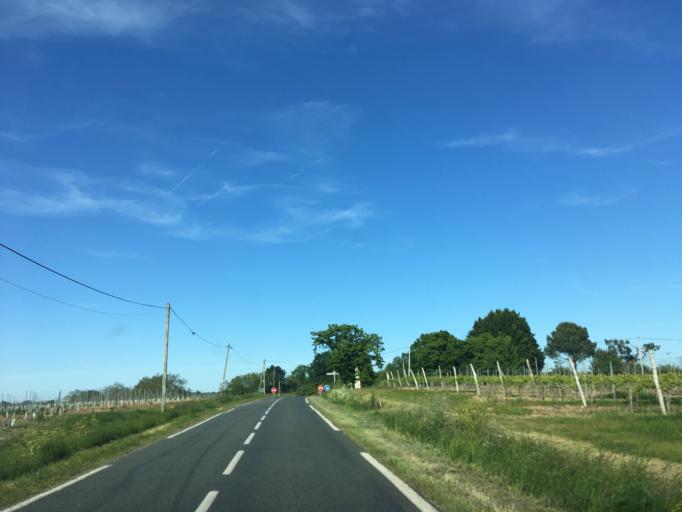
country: FR
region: Poitou-Charentes
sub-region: Departement de la Charente-Maritime
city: Mirambeau
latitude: 45.3552
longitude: -0.5750
